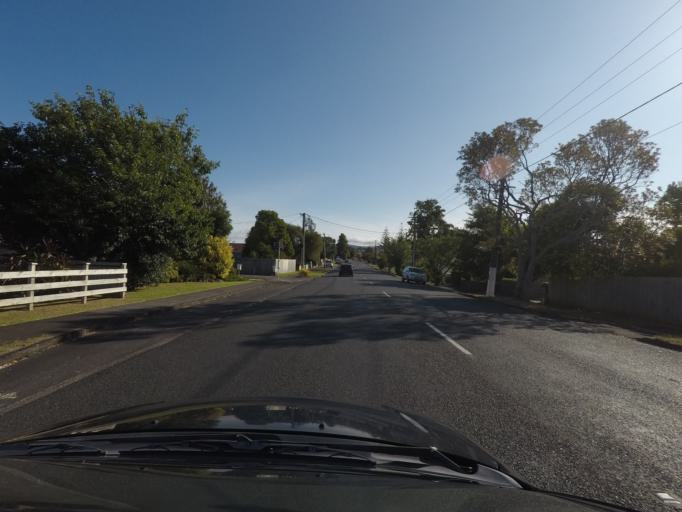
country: NZ
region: Auckland
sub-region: Auckland
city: Rosebank
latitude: -36.8646
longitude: 174.6097
